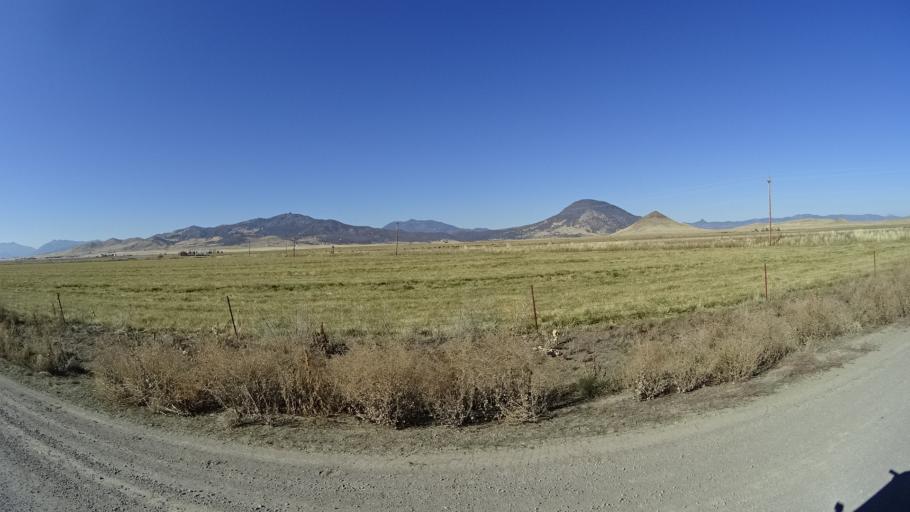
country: US
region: California
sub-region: Siskiyou County
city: Montague
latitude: 41.7921
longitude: -122.4568
